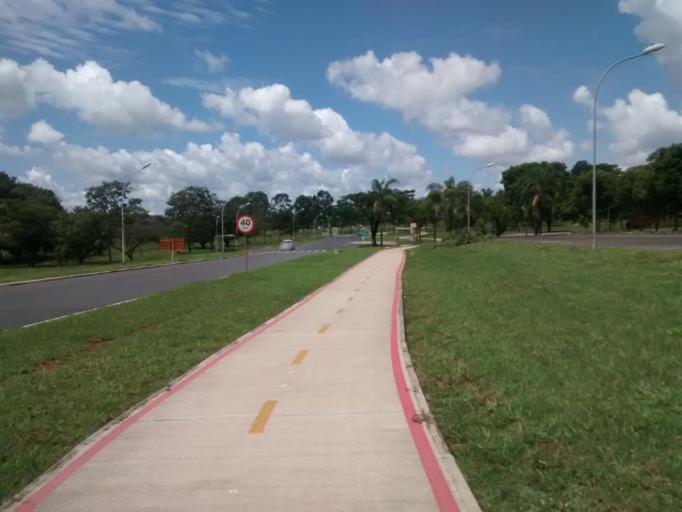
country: BR
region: Federal District
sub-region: Brasilia
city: Brasilia
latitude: -15.7615
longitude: -47.8663
